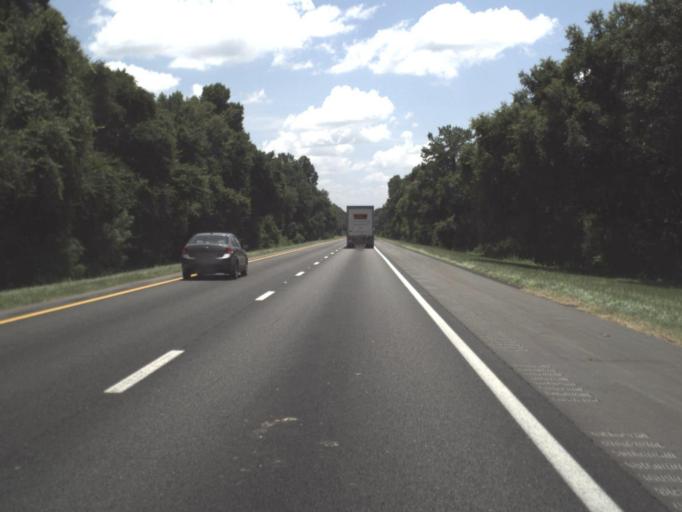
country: US
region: Florida
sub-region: Madison County
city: Madison
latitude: 30.4099
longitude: -83.4183
